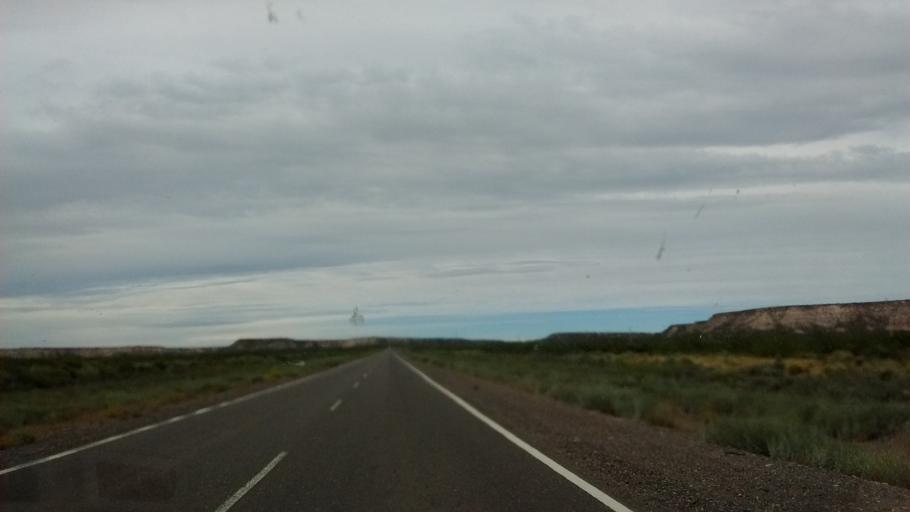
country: AR
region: Rio Negro
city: Catriel
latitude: -38.1828
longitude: -67.9578
